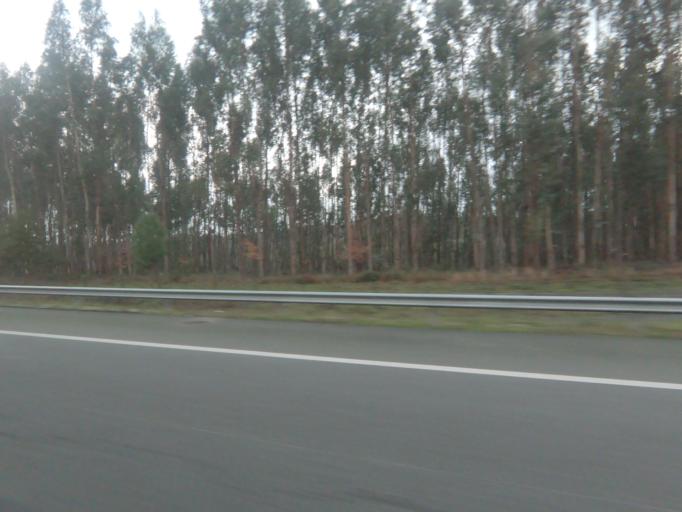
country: PT
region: Braga
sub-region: Barcelos
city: Galegos
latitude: 41.6314
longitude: -8.5622
